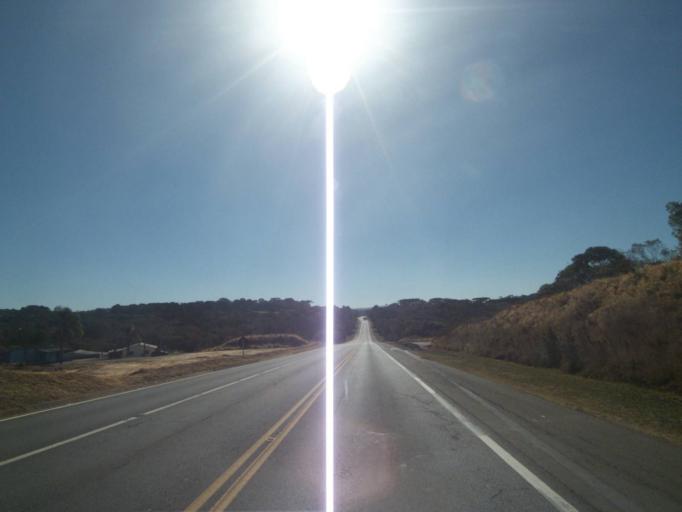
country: BR
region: Parana
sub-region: Tibagi
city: Tibagi
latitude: -24.7419
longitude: -50.5377
